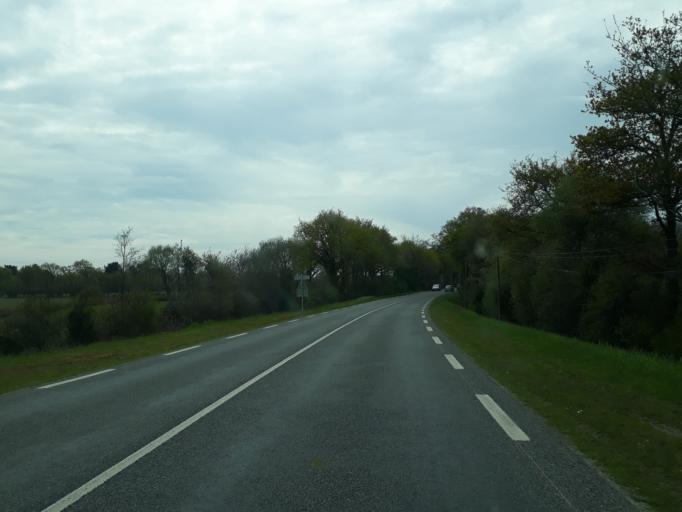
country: FR
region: Pays de la Loire
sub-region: Departement de la Loire-Atlantique
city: Saint-Molf
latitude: 47.3610
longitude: -2.4132
